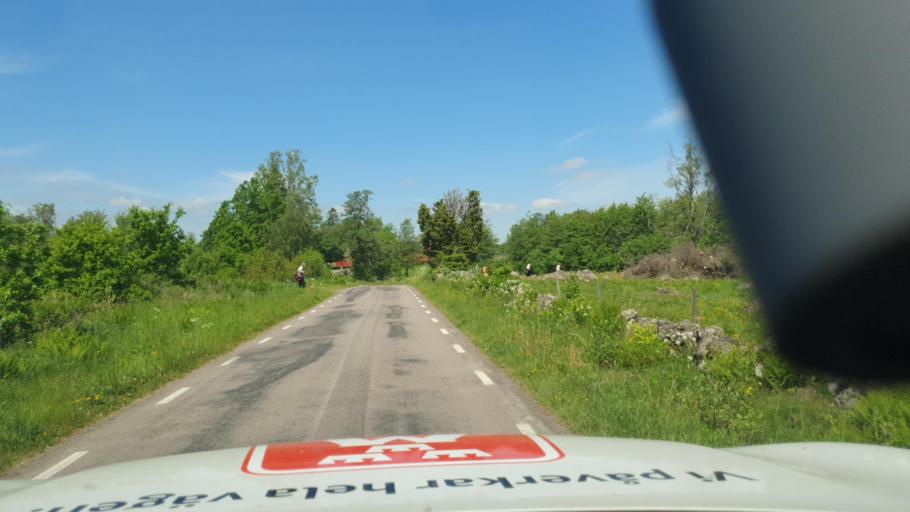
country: SE
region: Vaestra Goetaland
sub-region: Herrljunga Kommun
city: Herrljunga
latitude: 58.1439
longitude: 13.0717
